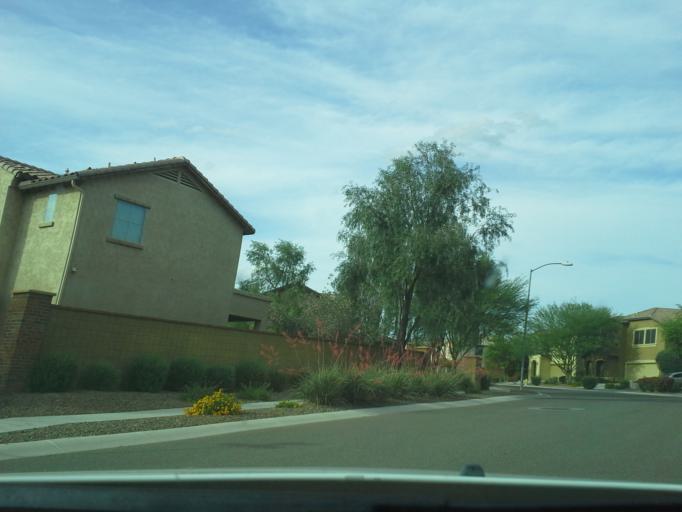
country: US
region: Arizona
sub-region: Maricopa County
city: Peoria
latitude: 33.6318
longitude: -112.2164
